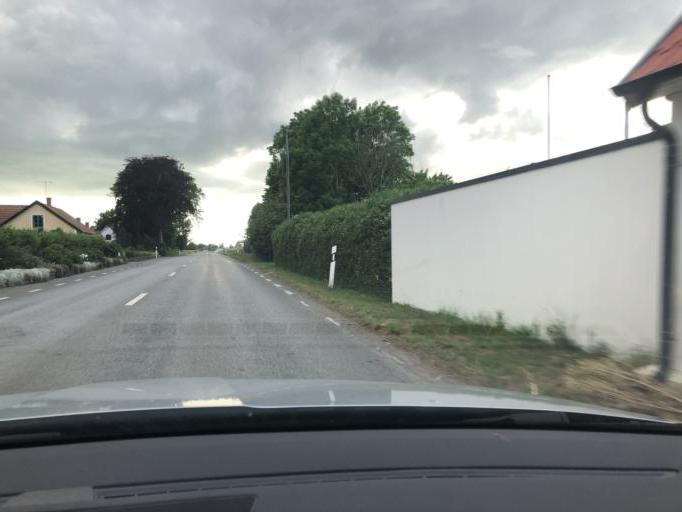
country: SE
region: Skane
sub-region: Simrishamns Kommun
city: Simrishamn
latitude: 55.5285
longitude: 14.2469
